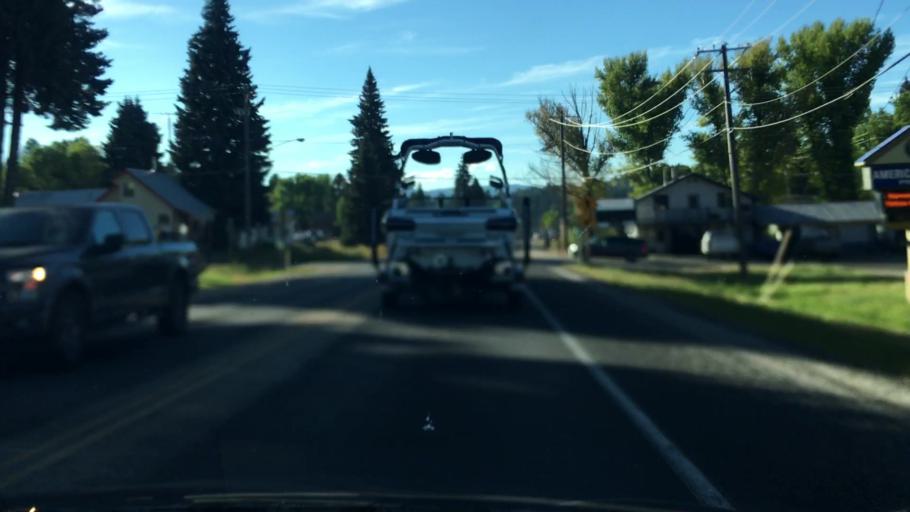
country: US
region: Idaho
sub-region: Valley County
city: Cascade
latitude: 44.5122
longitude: -116.0381
